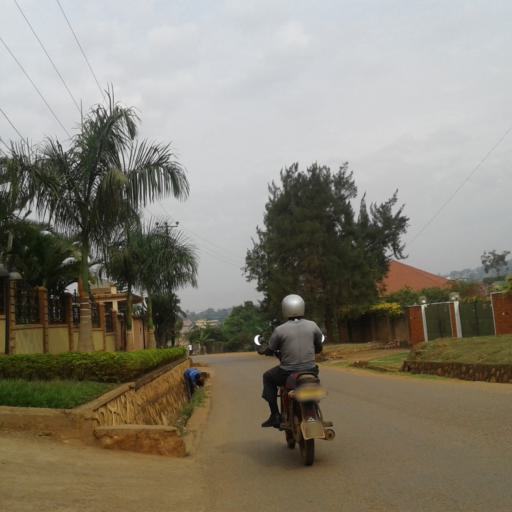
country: UG
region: Central Region
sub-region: Kampala District
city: Kampala
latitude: 0.2773
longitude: 32.6167
